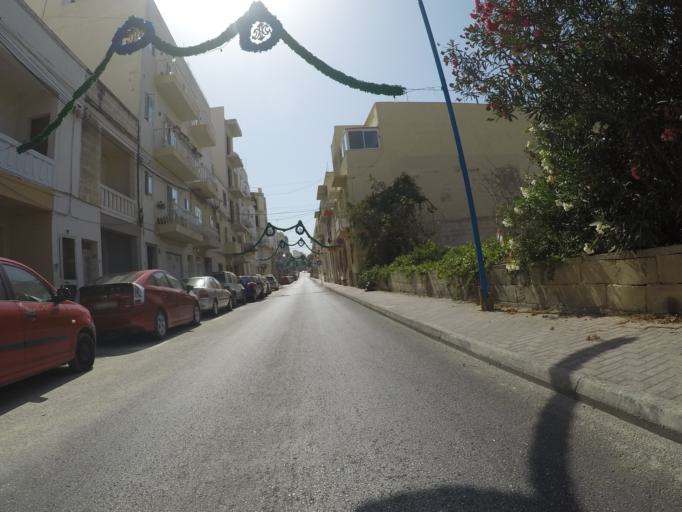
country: MT
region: Saint Paul's Bay
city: San Pawl il-Bahar
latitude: 35.9483
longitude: 14.4011
